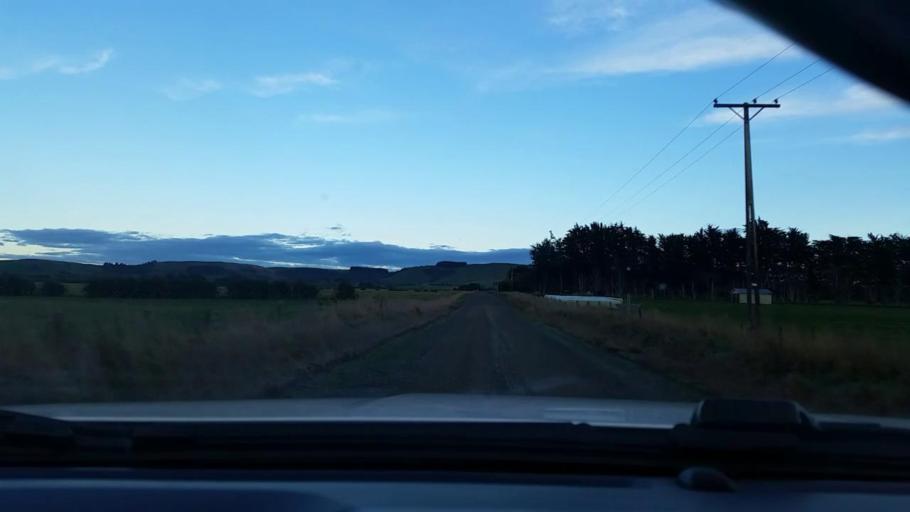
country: NZ
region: Southland
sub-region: Southland District
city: Winton
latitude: -46.1078
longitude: 168.4448
